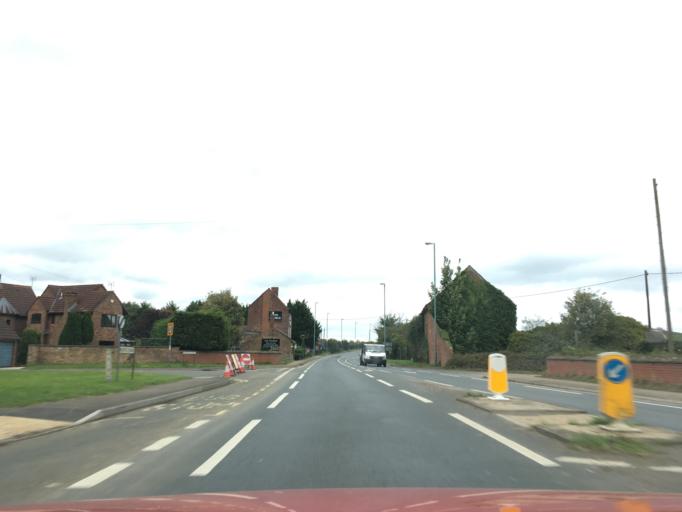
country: GB
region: England
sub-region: Gloucestershire
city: Dursley
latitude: 51.7316
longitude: -2.3645
